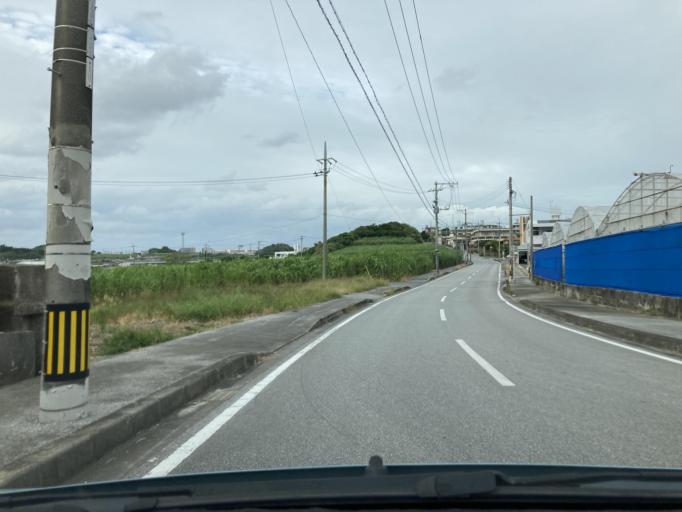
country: JP
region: Okinawa
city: Tomigusuku
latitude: 26.1527
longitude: 127.6973
